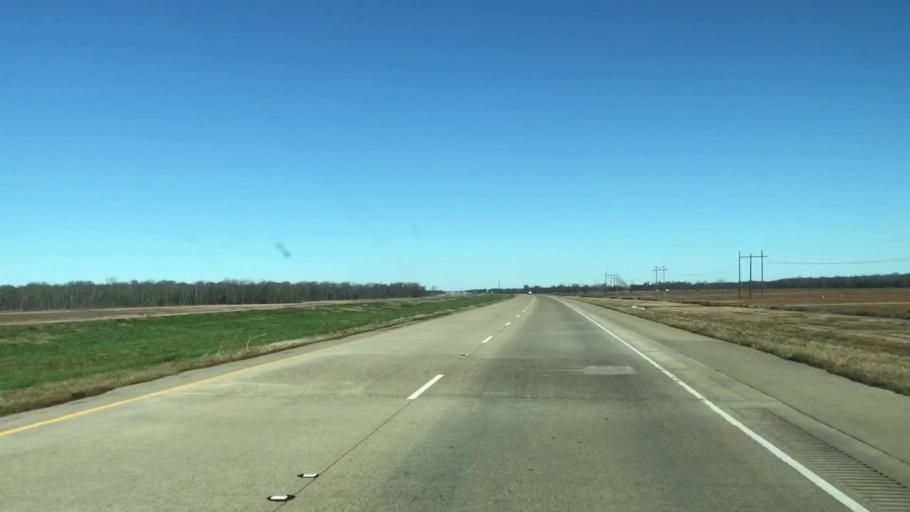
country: US
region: Louisiana
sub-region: Caddo Parish
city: Blanchard
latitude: 32.6505
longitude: -93.8407
